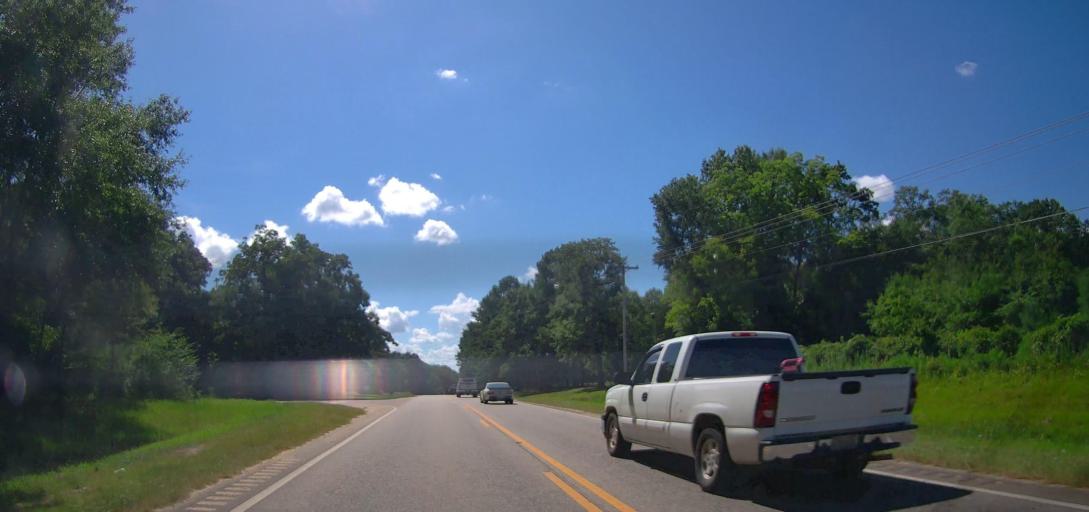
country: US
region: Alabama
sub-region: Elmore County
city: Tallassee
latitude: 32.3785
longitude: -85.8621
